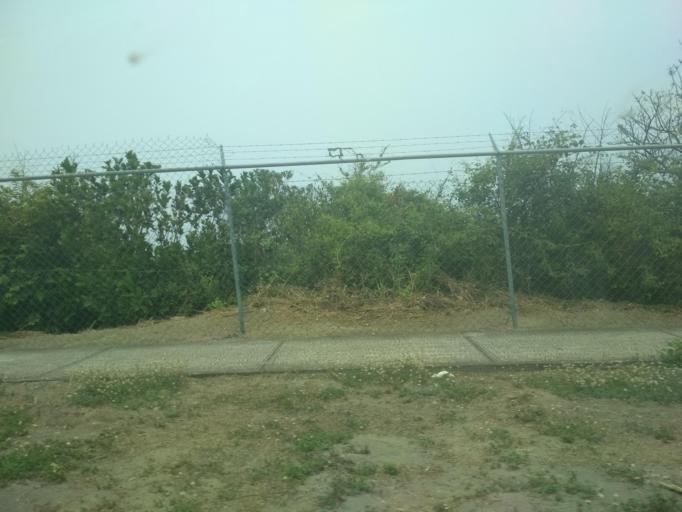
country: MX
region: Veracruz
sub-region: Alvarado
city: Playa de la Libertad
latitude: 19.0665
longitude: -96.0794
